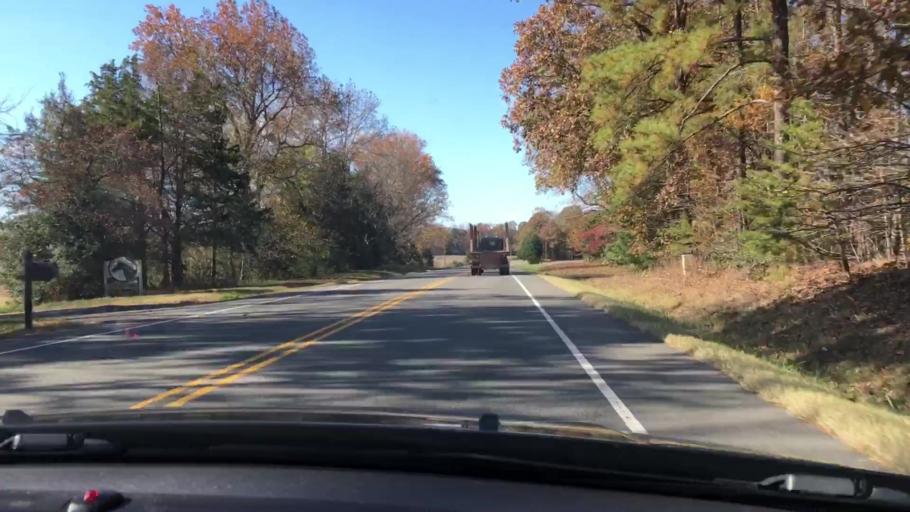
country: US
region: Virginia
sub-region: King William County
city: Central Garage
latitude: 37.7757
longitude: -77.1603
